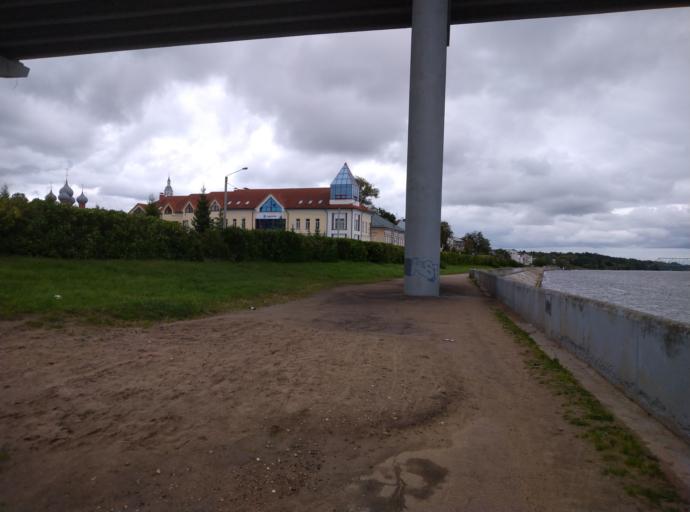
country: RU
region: Kostroma
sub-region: Kostromskoy Rayon
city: Kostroma
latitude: 57.7558
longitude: 40.9429
